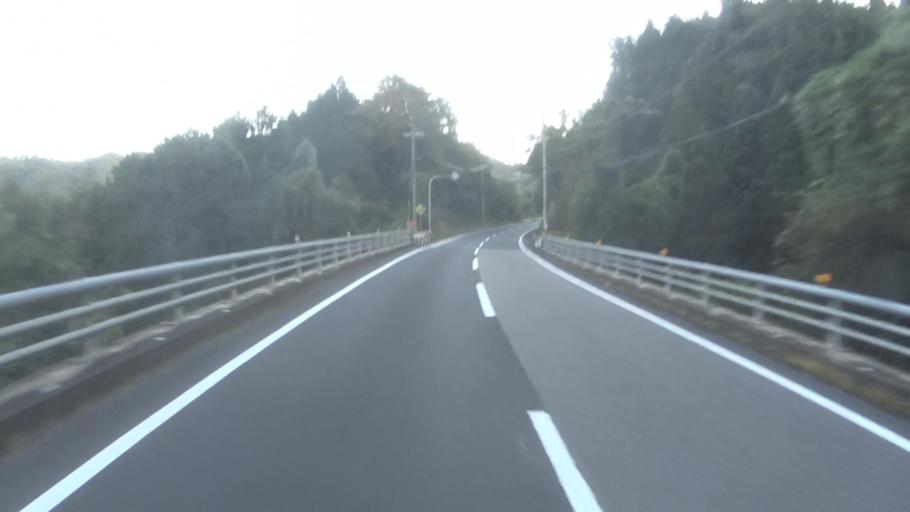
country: JP
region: Kyoto
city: Ayabe
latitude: 35.2819
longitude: 135.2700
